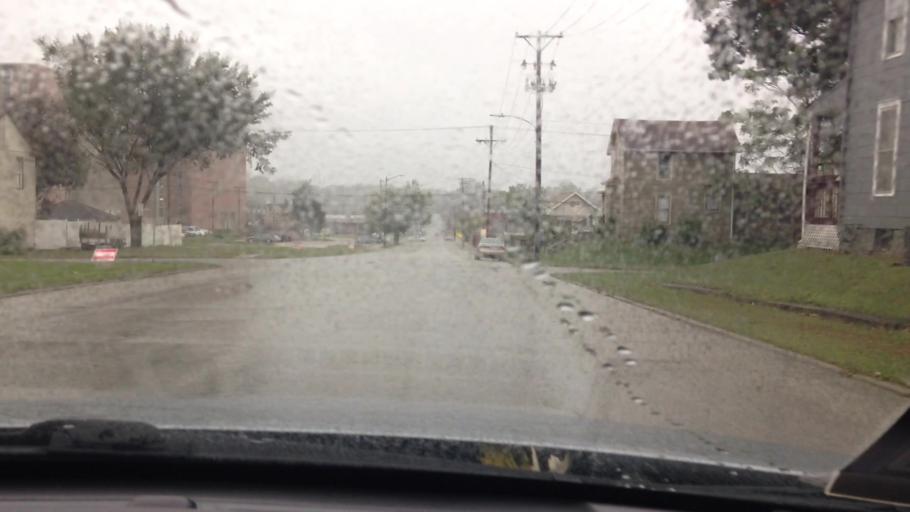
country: US
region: Kansas
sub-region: Leavenworth County
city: Leavenworth
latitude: 39.3214
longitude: -94.9129
